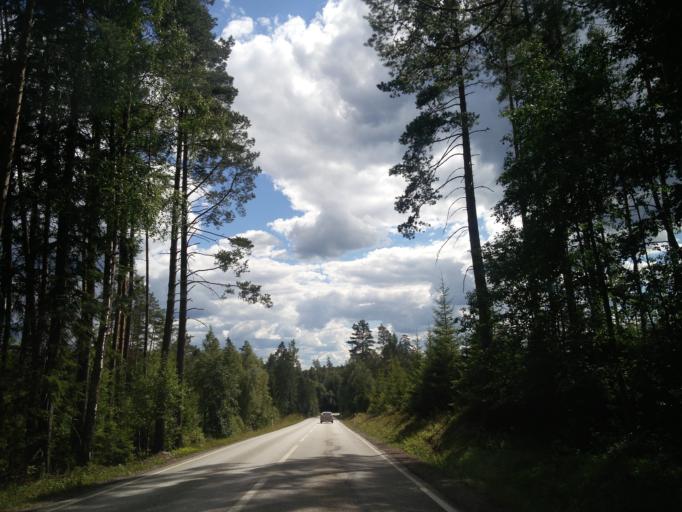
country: SE
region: OErebro
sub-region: Ljusnarsbergs Kommun
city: Kopparberg
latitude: 59.8467
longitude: 14.9981
